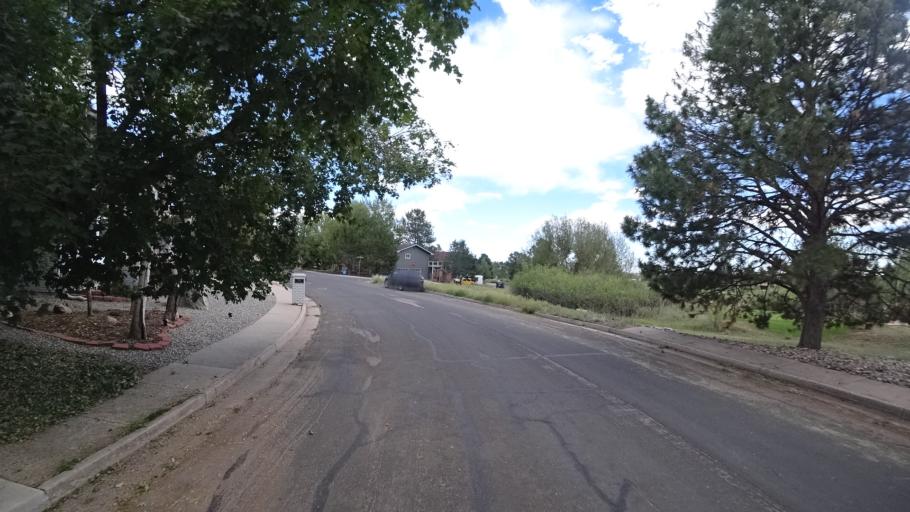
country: US
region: Colorado
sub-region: El Paso County
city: Stratmoor
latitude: 38.7809
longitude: -104.8302
